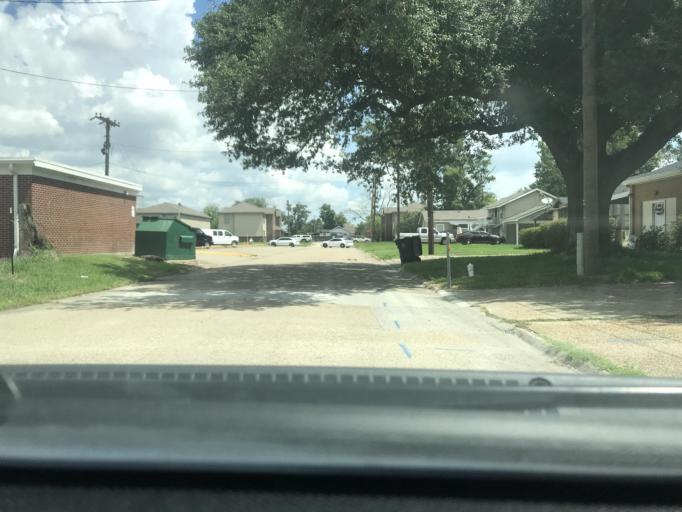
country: US
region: Louisiana
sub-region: Calcasieu Parish
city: Lake Charles
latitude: 30.2009
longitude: -93.2175
